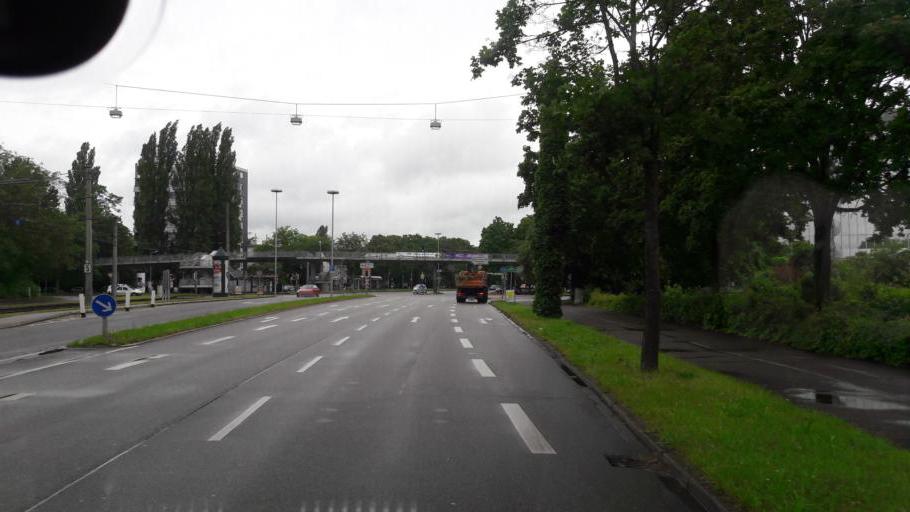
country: DE
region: Baden-Wuerttemberg
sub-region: Karlsruhe Region
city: Karlsruhe
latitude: 48.9798
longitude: 8.4048
